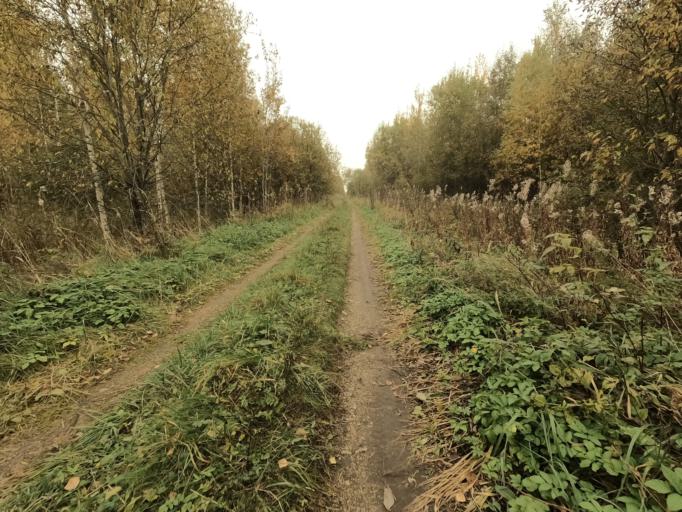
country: RU
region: Novgorod
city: Pankovka
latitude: 58.8794
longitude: 30.9423
